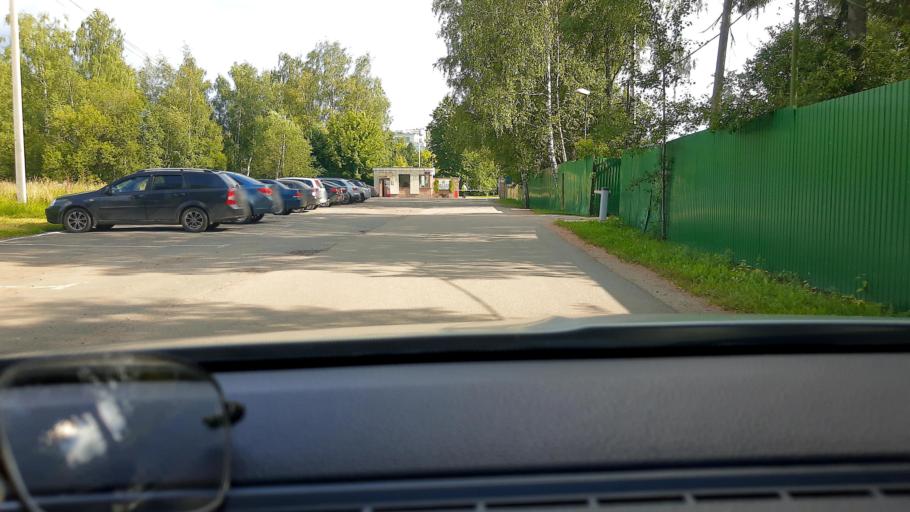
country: RU
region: Moskovskaya
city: Marfino
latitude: 56.0963
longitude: 37.5367
